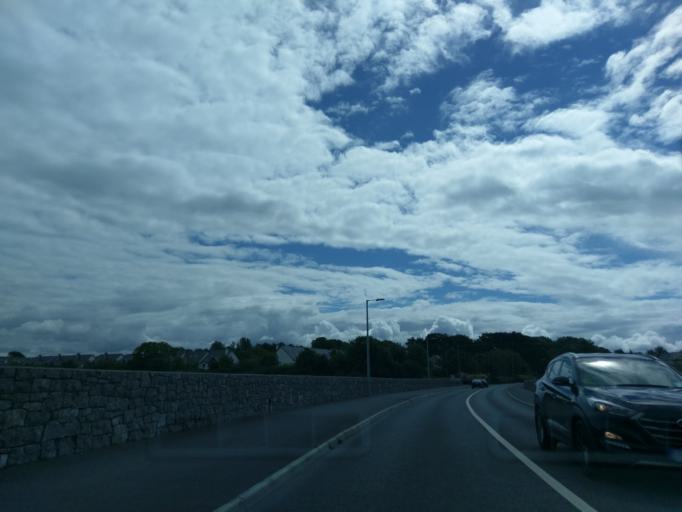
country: IE
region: Connaught
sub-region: County Galway
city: Oranmore
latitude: 53.2603
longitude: -8.9328
